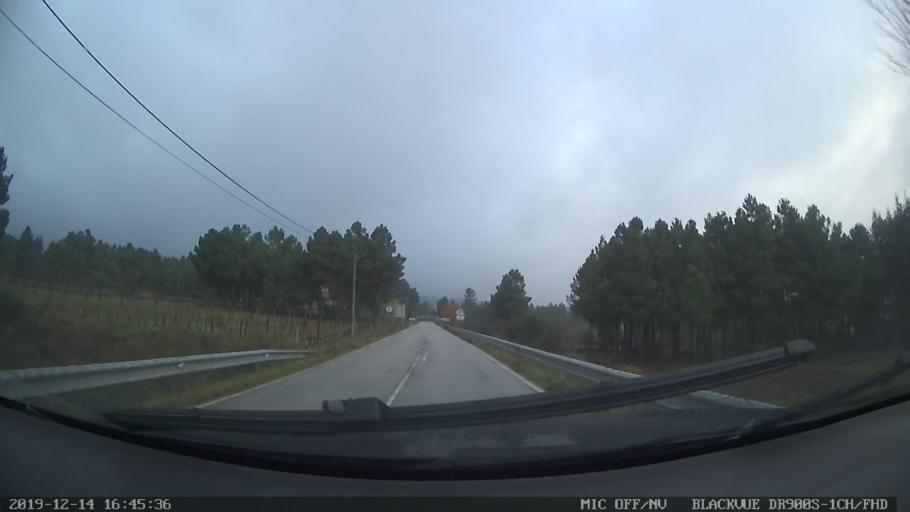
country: PT
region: Vila Real
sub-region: Murca
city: Murca
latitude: 41.3998
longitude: -7.4889
